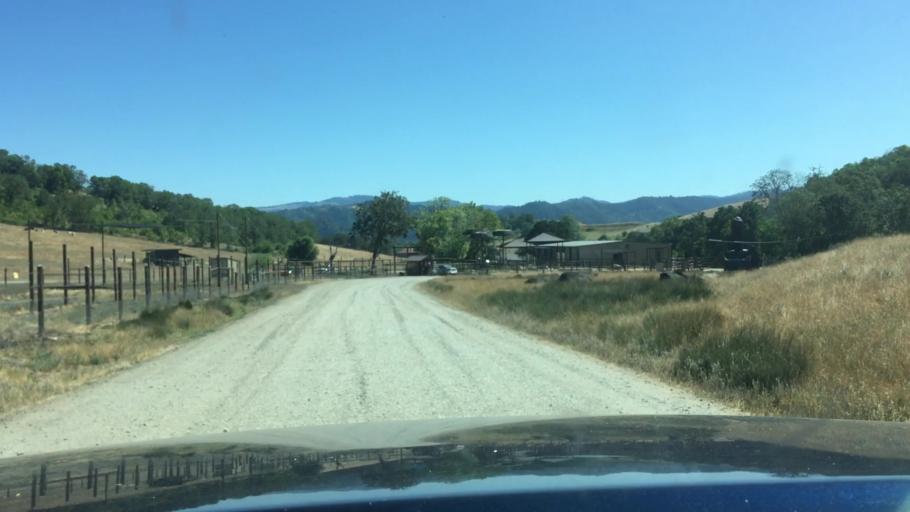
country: US
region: Oregon
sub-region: Douglas County
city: Winston
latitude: 43.1381
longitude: -123.4324
